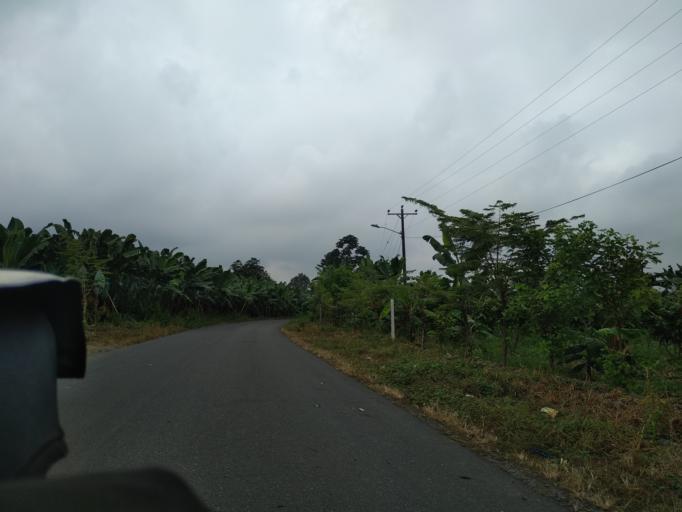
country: EC
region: Los Rios
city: Quevedo
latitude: -0.9755
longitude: -79.3542
